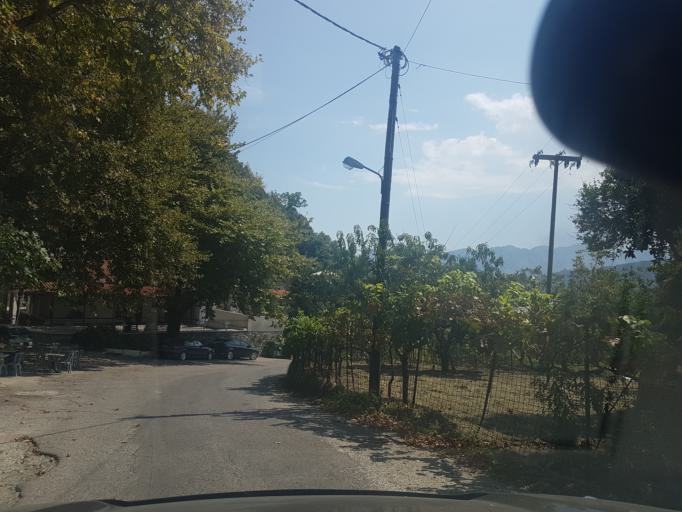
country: GR
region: Central Greece
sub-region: Nomos Evvoias
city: Kymi
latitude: 38.6500
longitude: 23.9043
